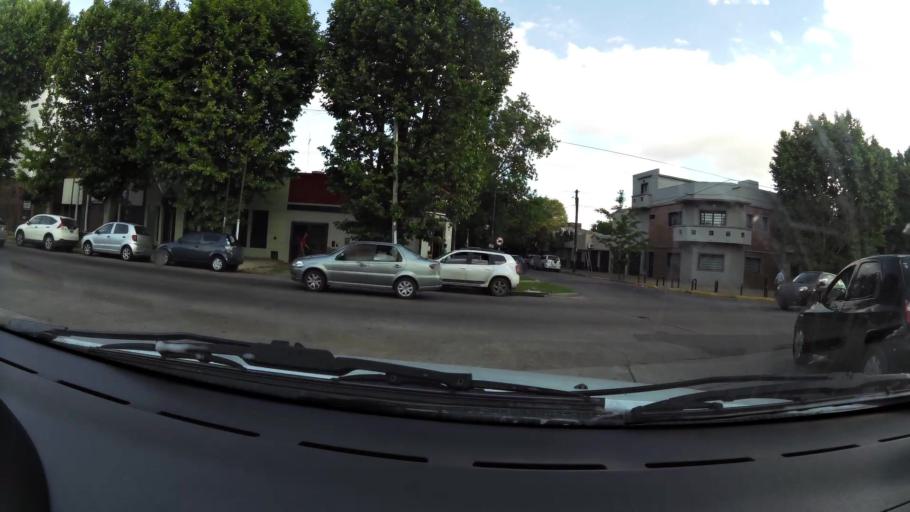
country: AR
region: Buenos Aires
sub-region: Partido de La Plata
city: La Plata
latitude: -34.8957
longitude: -57.9637
